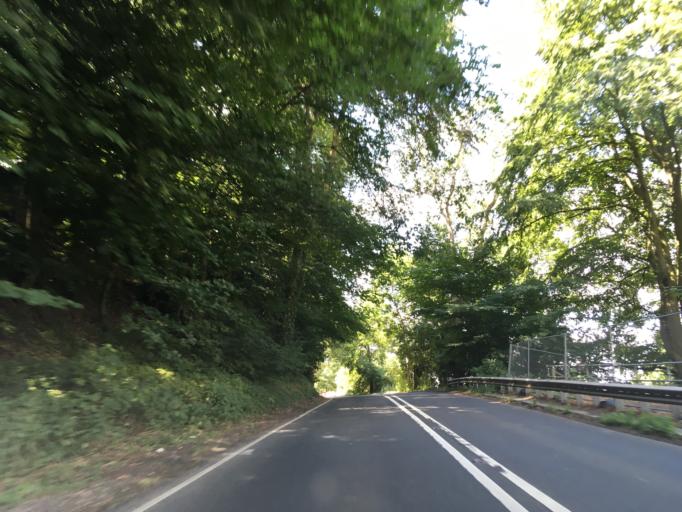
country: GB
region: England
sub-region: Gloucestershire
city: Churchdown
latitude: 51.8341
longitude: -2.1645
